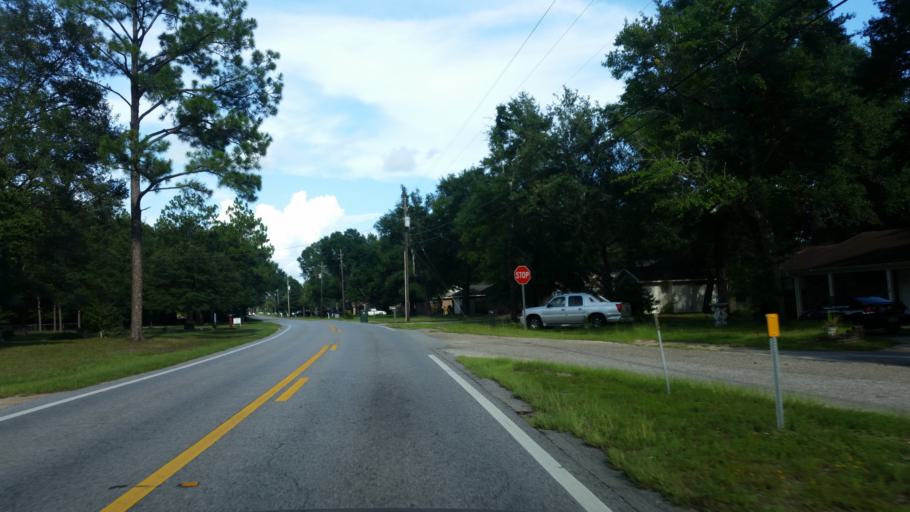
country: US
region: Florida
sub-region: Santa Rosa County
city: Milton
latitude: 30.6206
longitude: -87.0727
